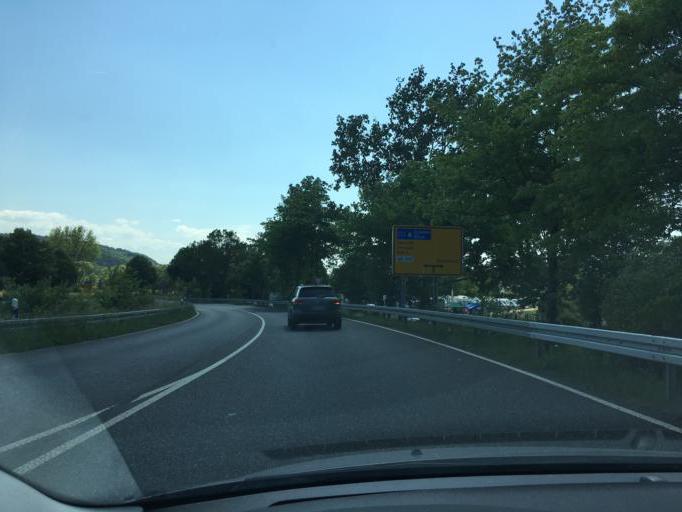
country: DE
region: Hesse
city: Breitenbach
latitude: 50.9608
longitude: 9.7889
